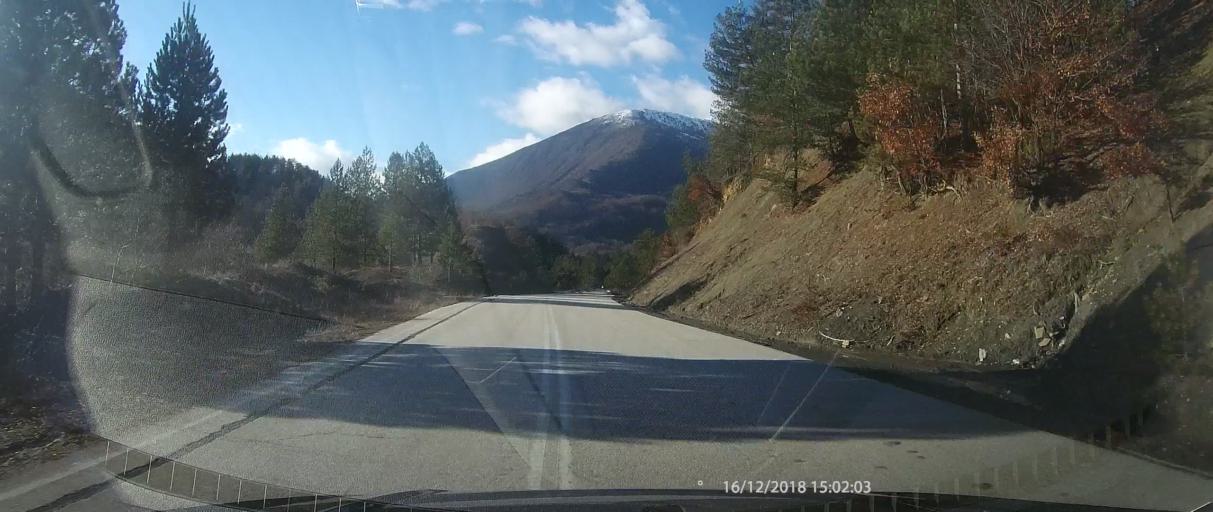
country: GR
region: West Macedonia
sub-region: Nomos Kastorias
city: Nestorio
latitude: 40.2271
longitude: 21.0000
